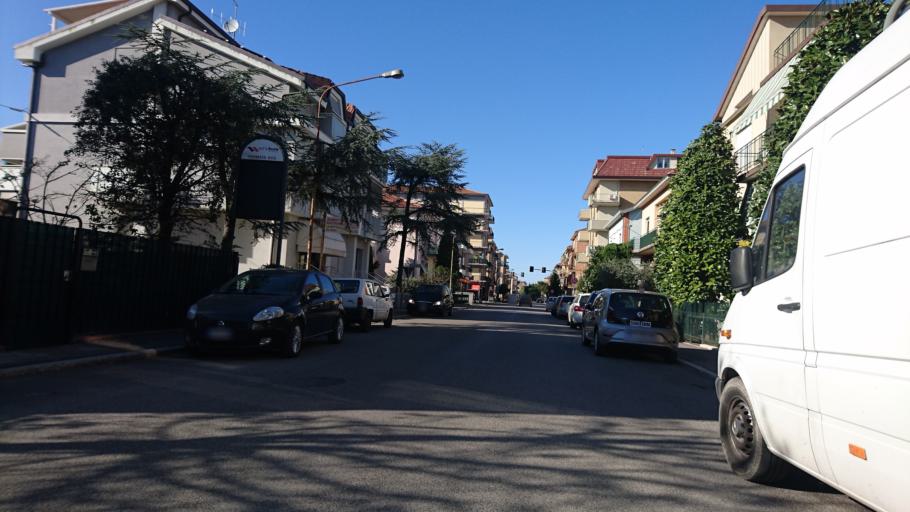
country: IT
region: The Marches
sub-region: Provincia di Pesaro e Urbino
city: Pesaro
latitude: 43.8955
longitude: 12.9064
